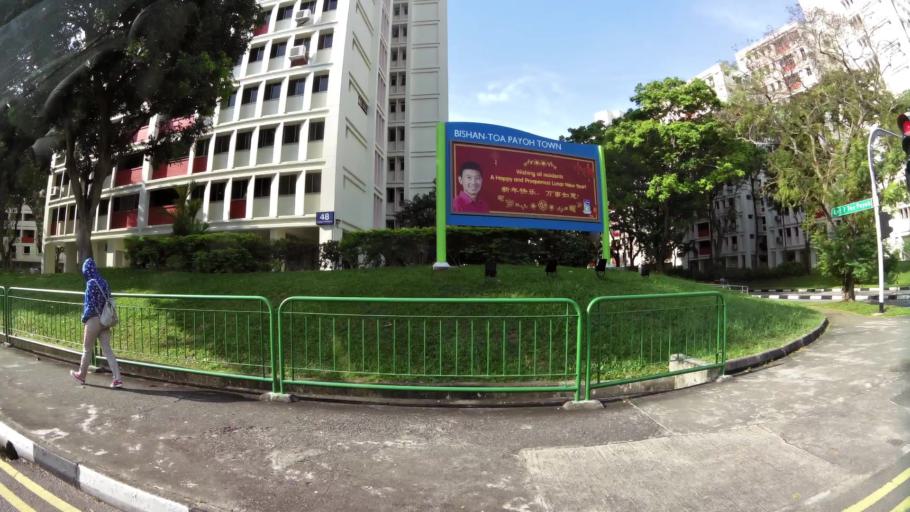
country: SG
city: Singapore
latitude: 1.3377
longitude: 103.8538
